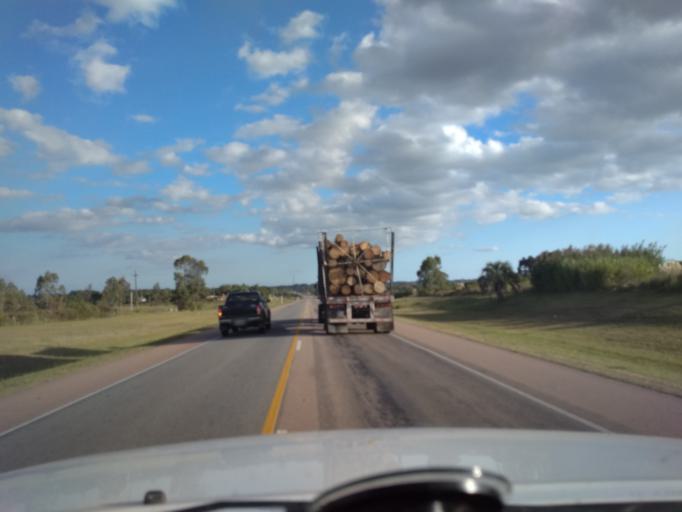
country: UY
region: Canelones
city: Canelones
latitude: -34.4893
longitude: -56.2819
